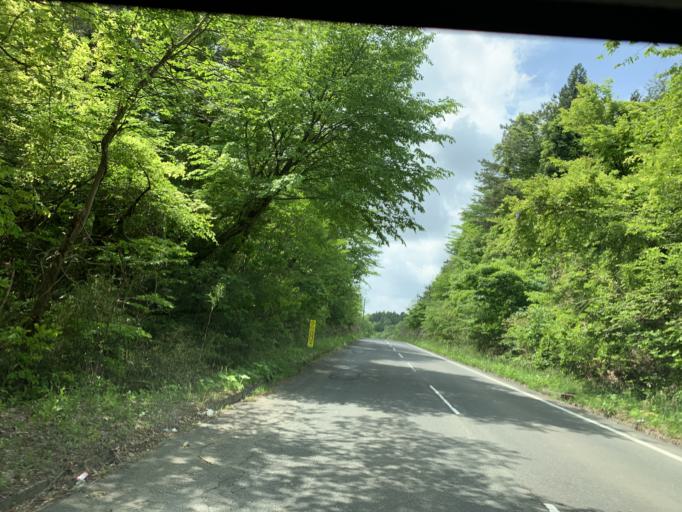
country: JP
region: Miyagi
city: Furukawa
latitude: 38.7629
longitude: 140.9406
